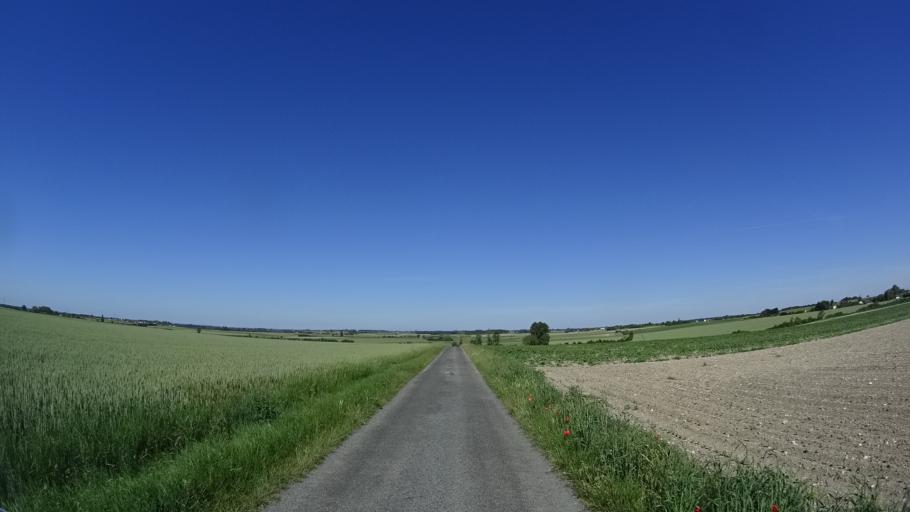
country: FR
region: Pays de la Loire
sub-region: Departement de Maine-et-Loire
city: Doue-la-Fontaine
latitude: 47.2503
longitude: -0.2822
